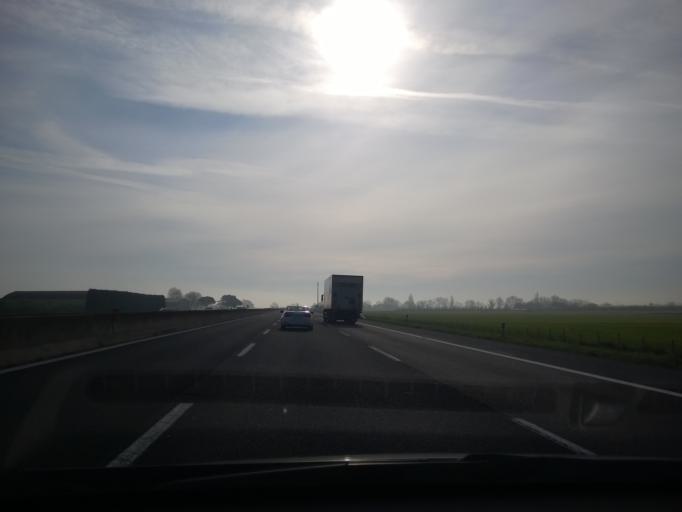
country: IT
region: Emilia-Romagna
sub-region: Provincia di Bologna
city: Castel Guelfo di Bologna
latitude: 44.4120
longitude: 11.6537
